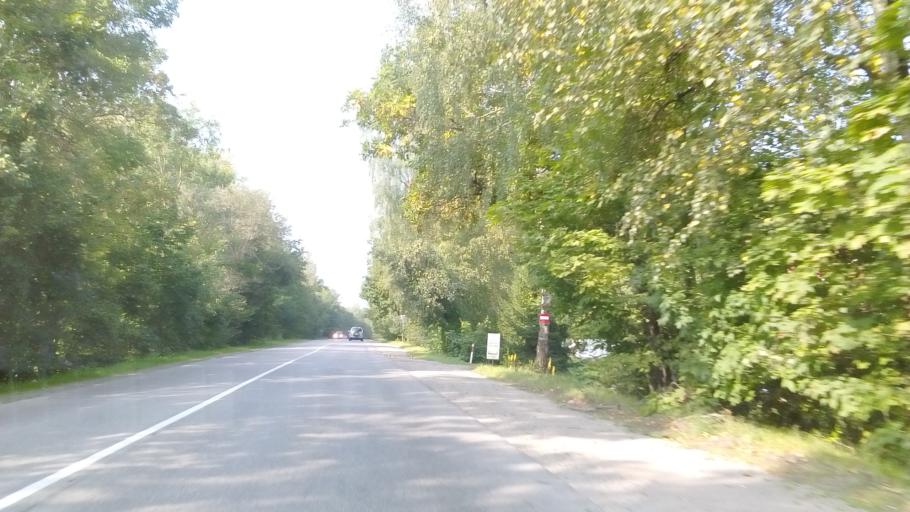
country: LT
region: Alytaus apskritis
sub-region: Alytus
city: Alytus
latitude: 54.3866
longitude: 24.0136
